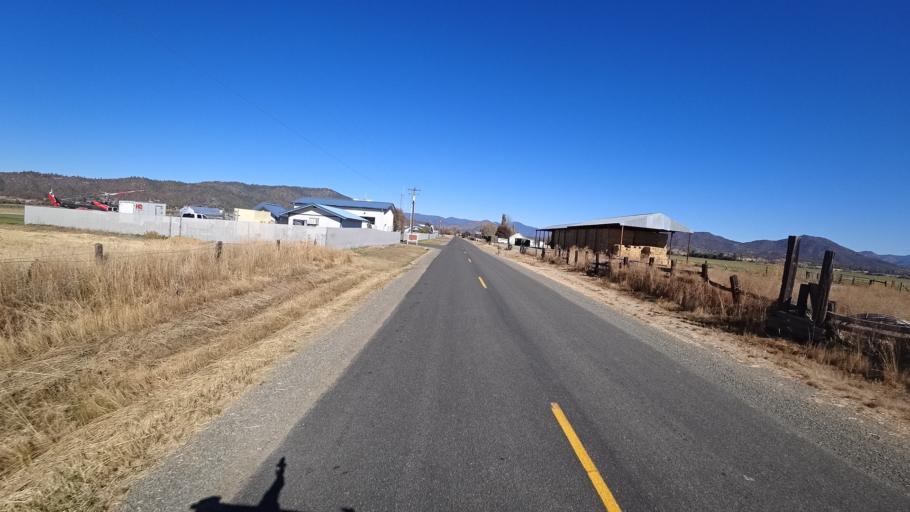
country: US
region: California
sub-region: Siskiyou County
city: Yreka
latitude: 41.5558
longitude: -122.8531
